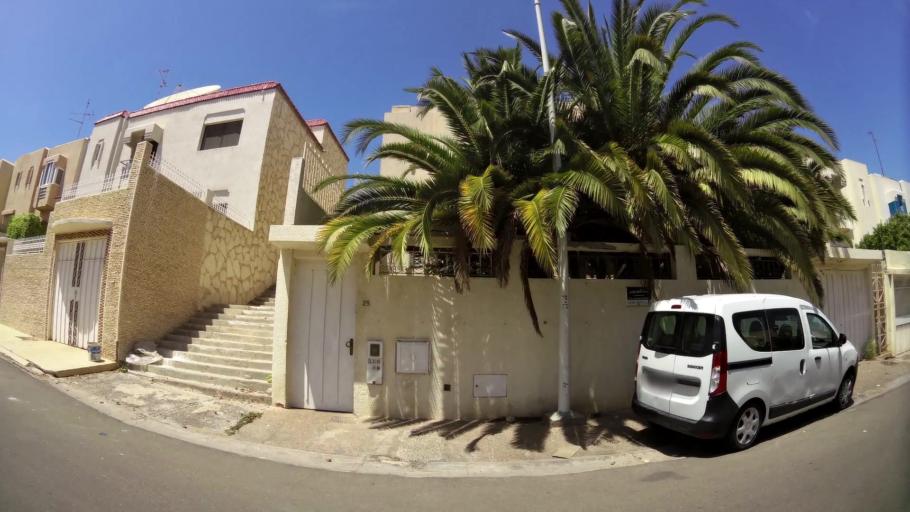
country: MA
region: Souss-Massa-Draa
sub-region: Agadir-Ida-ou-Tnan
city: Agadir
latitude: 30.4348
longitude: -9.5825
